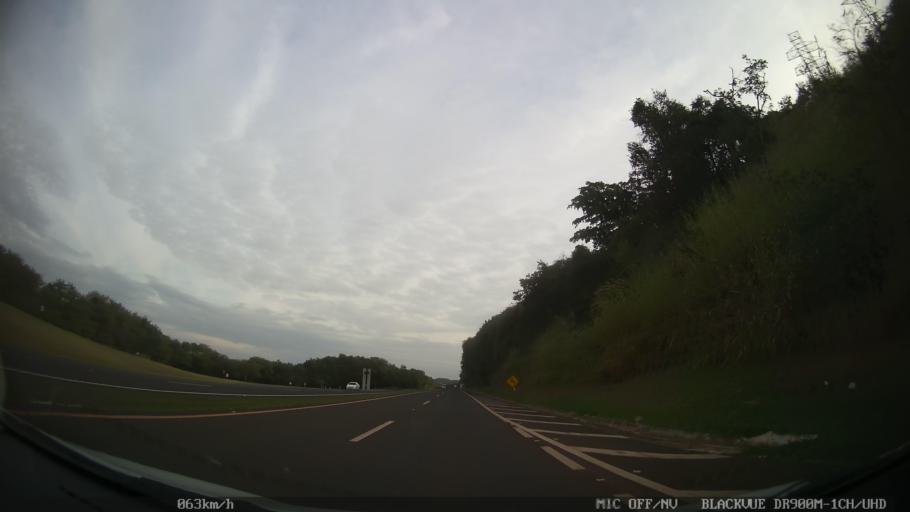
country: BR
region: Sao Paulo
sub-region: Piracicaba
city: Piracicaba
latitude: -22.6879
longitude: -47.5840
